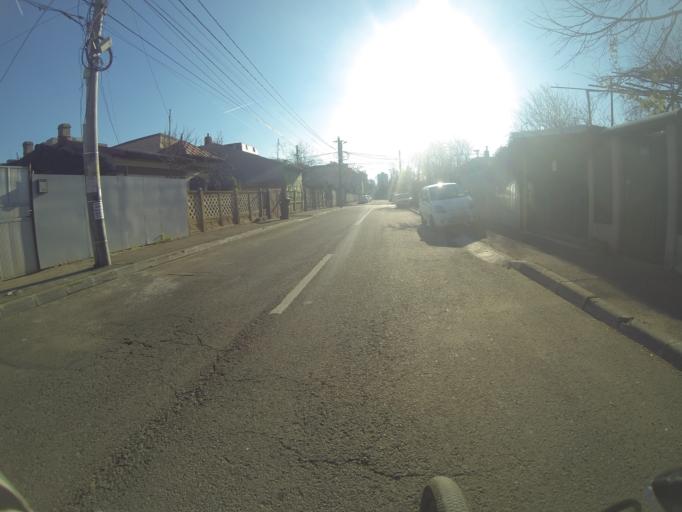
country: RO
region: Bucuresti
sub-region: Municipiul Bucuresti
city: Bucuresti
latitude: 44.3973
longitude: 26.0677
